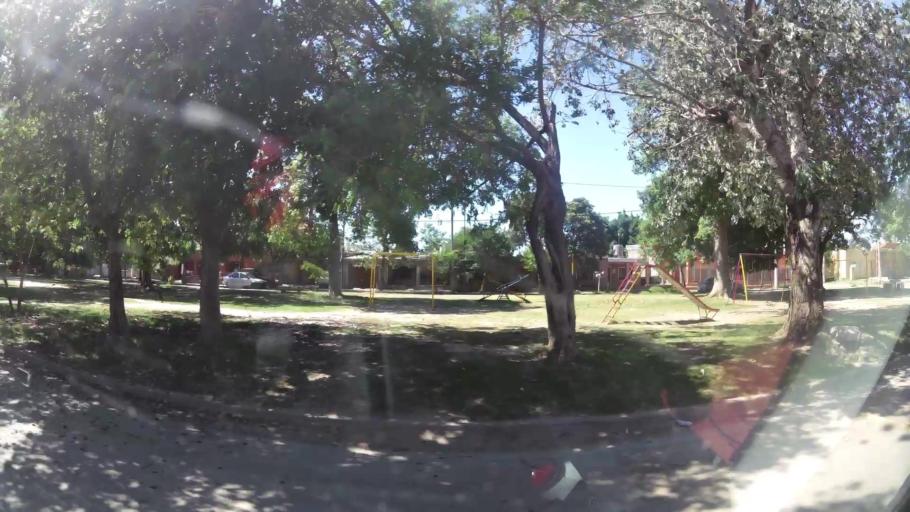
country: AR
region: Cordoba
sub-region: Departamento de Capital
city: Cordoba
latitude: -31.3696
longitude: -64.1318
